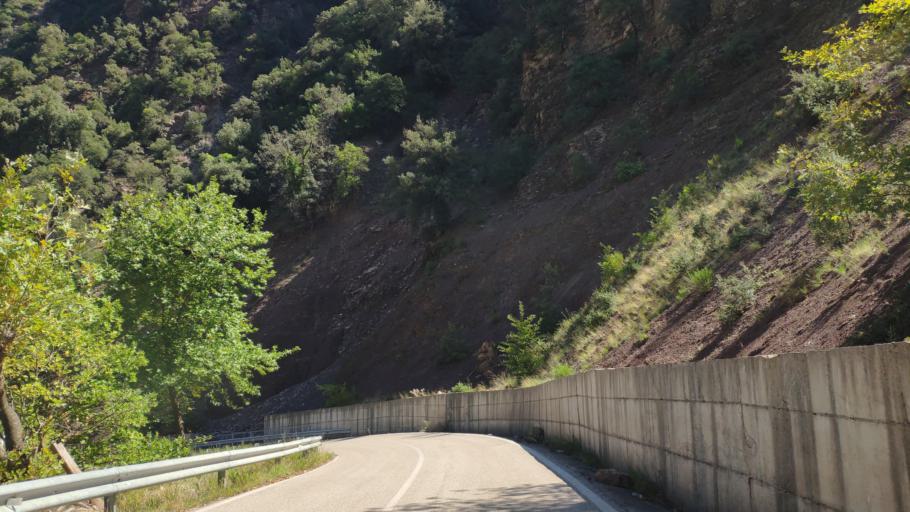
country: GR
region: Central Greece
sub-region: Nomos Evrytanias
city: Kerasochori
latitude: 39.0449
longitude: 21.5967
